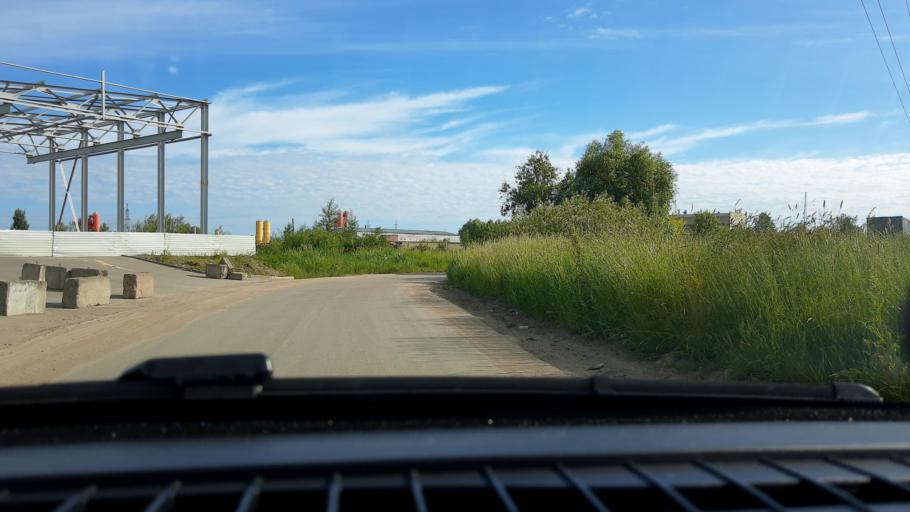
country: RU
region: Nizjnij Novgorod
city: Gorbatovka
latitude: 56.2715
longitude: 43.8493
